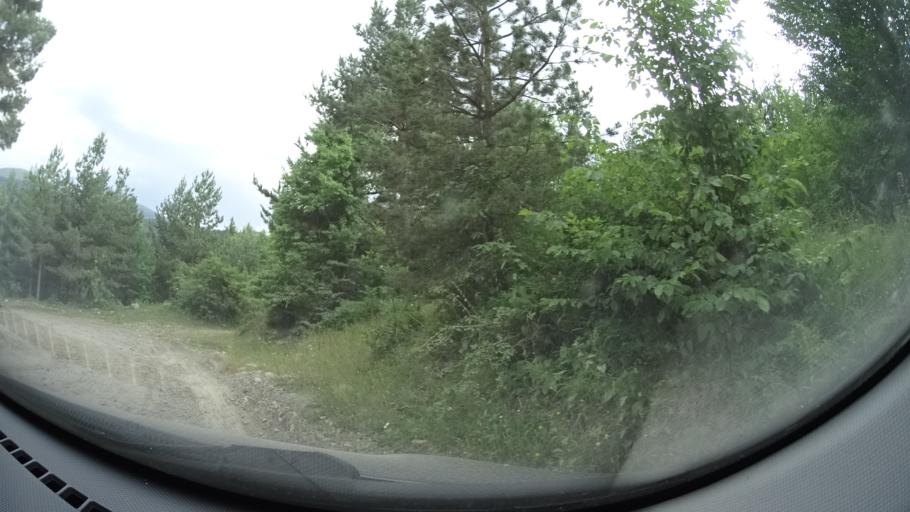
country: GE
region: Samtskhe-Javakheti
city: Adigeni
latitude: 41.6643
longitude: 42.6130
